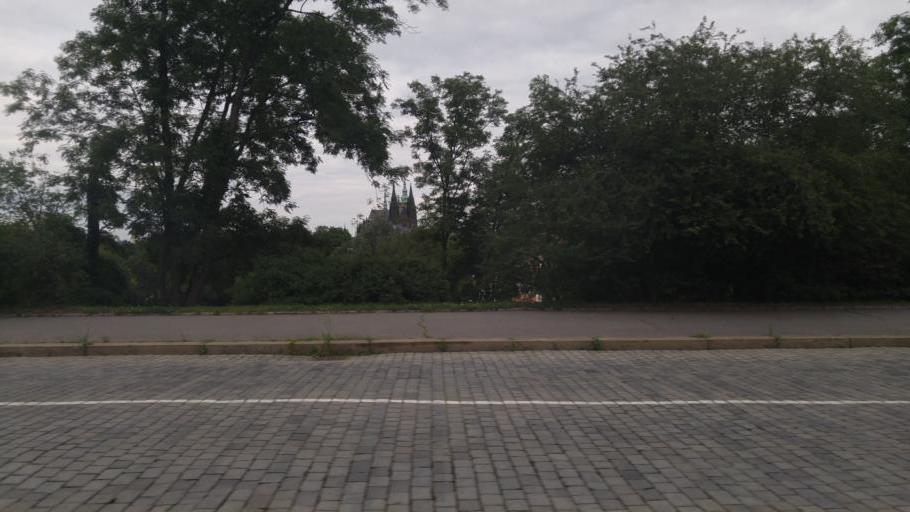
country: CZ
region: Praha
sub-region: Praha 1
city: Mala Strana
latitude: 50.0911
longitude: 14.3888
